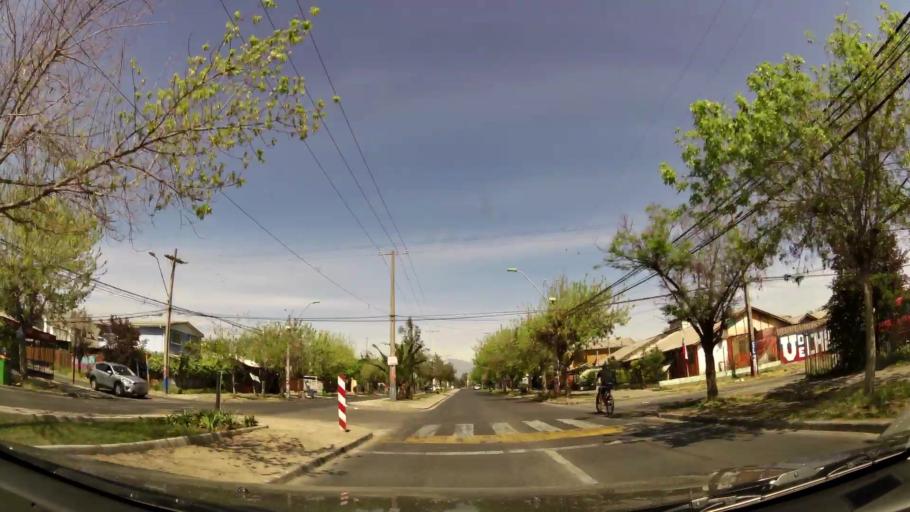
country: CL
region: Santiago Metropolitan
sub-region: Provincia de Cordillera
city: Puente Alto
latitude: -33.5741
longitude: -70.5654
